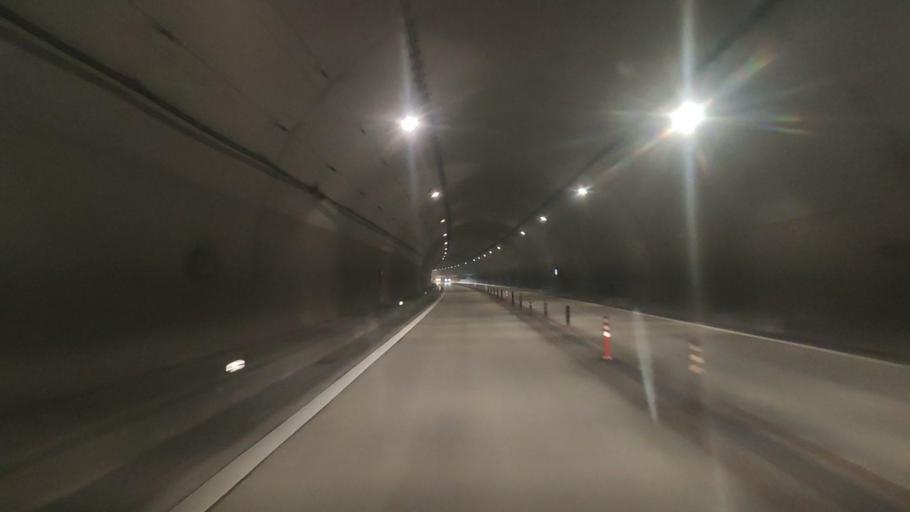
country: JP
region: Nagasaki
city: Shimabara
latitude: 32.7761
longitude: 130.3562
